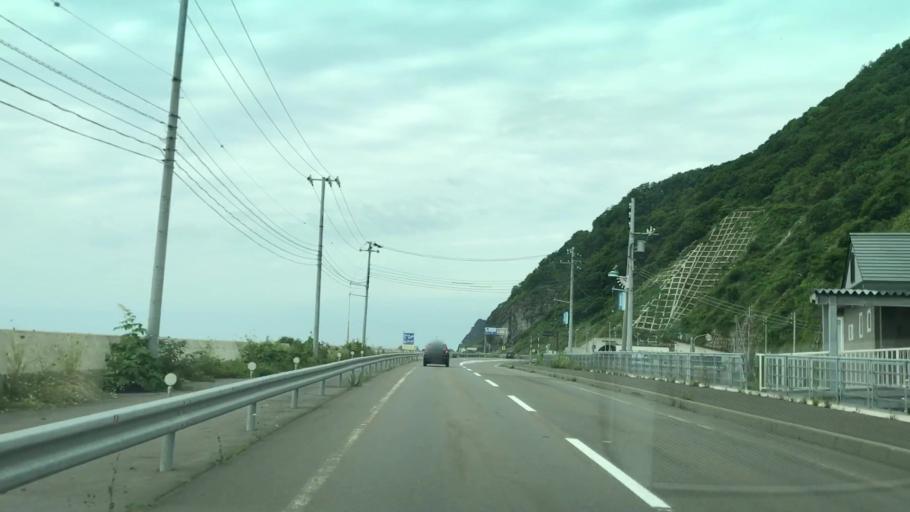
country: JP
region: Hokkaido
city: Iwanai
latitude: 43.1640
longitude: 140.3869
